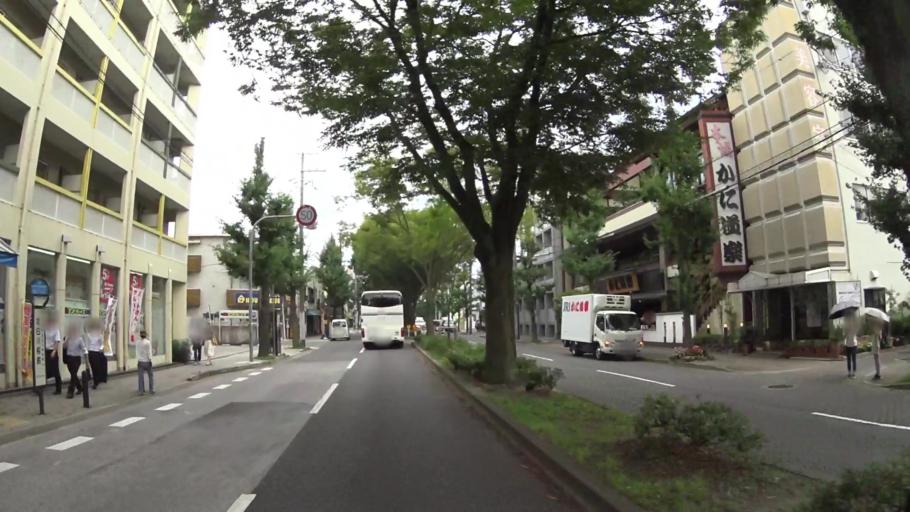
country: JP
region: Kyoto
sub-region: Kyoto-shi
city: Kamigyo-ku
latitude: 35.0300
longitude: 135.7914
